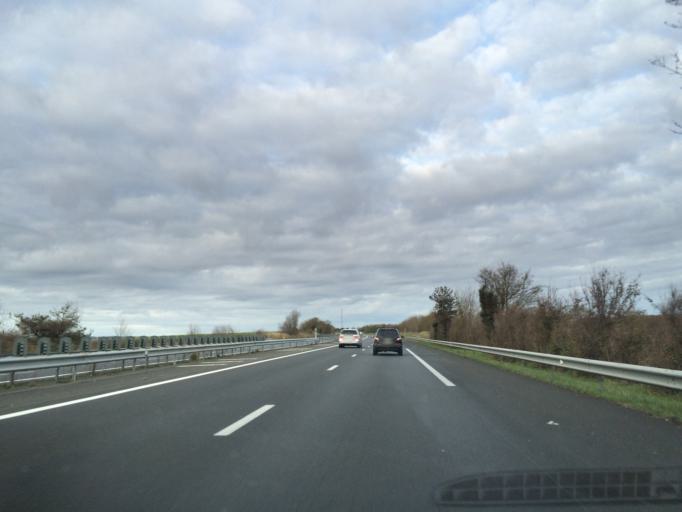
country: FR
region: Poitou-Charentes
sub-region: Departement de la Charente-Maritime
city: Saint-Jean-d'Angely
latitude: 46.0291
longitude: -0.5389
